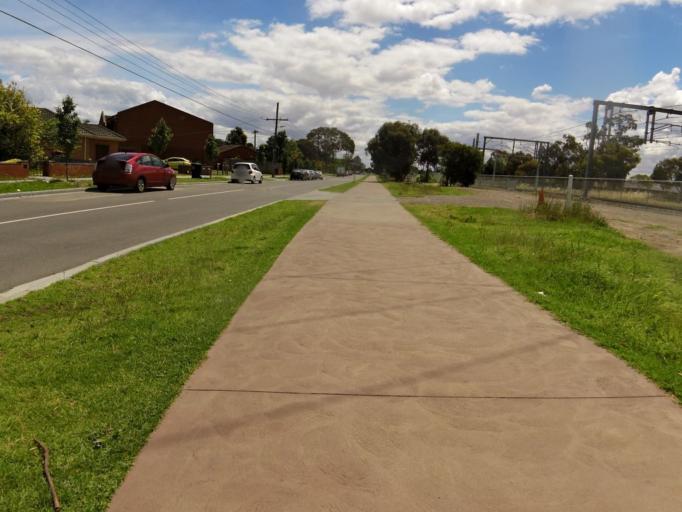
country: AU
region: Victoria
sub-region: Kingston
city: Clayton South
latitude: -37.9349
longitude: 145.1337
